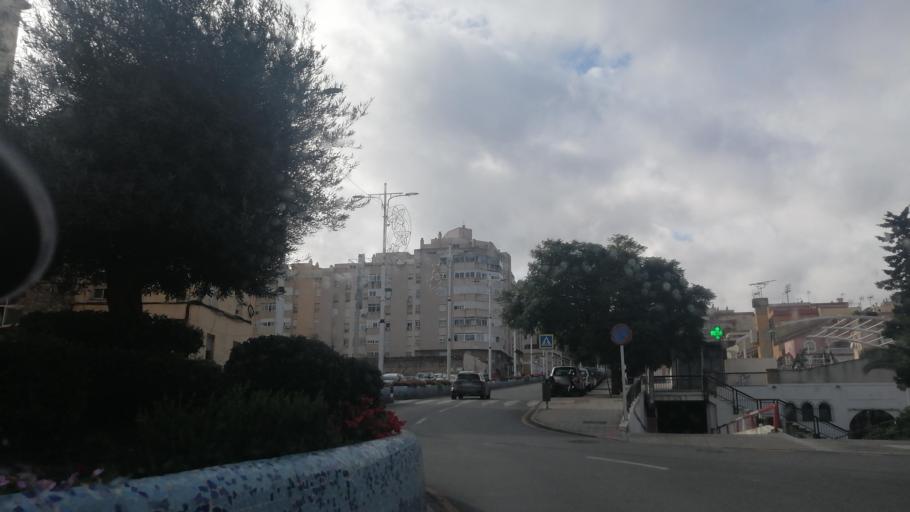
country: ES
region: Ceuta
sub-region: Ceuta
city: Ceuta
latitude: 35.8868
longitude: -5.3233
